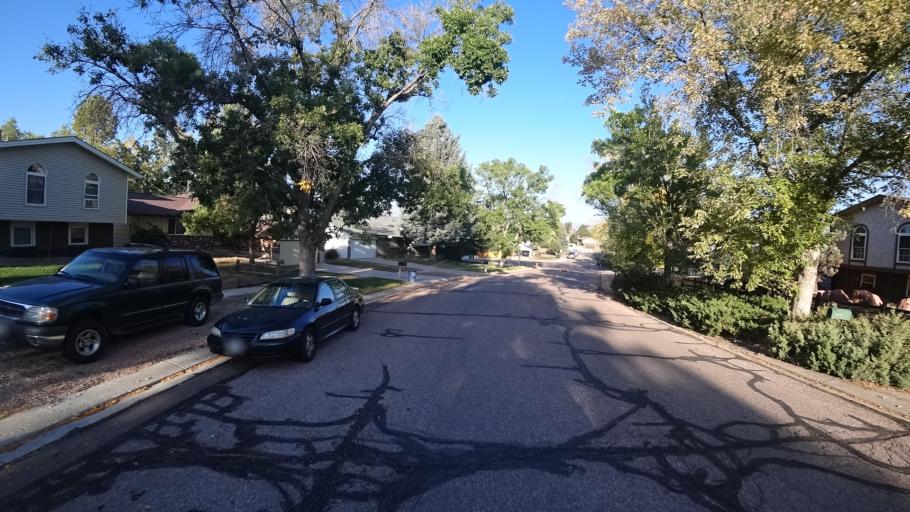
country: US
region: Colorado
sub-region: El Paso County
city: Cimarron Hills
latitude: 38.8847
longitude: -104.7488
